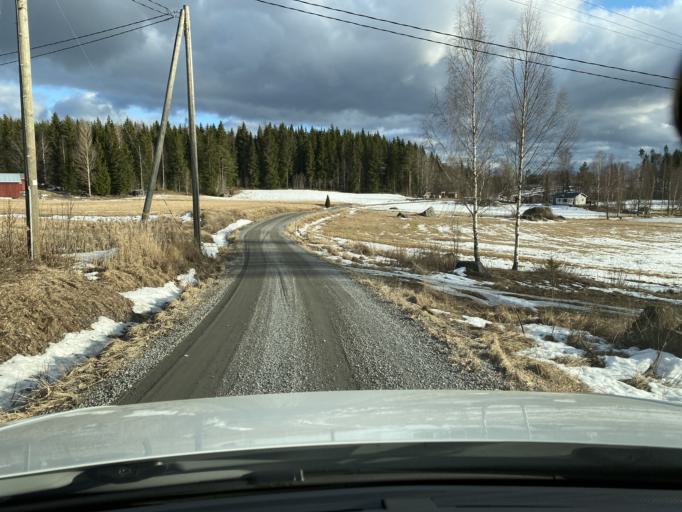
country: FI
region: Pirkanmaa
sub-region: Lounais-Pirkanmaa
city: Mouhijaervi
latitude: 61.4405
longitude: 22.9637
